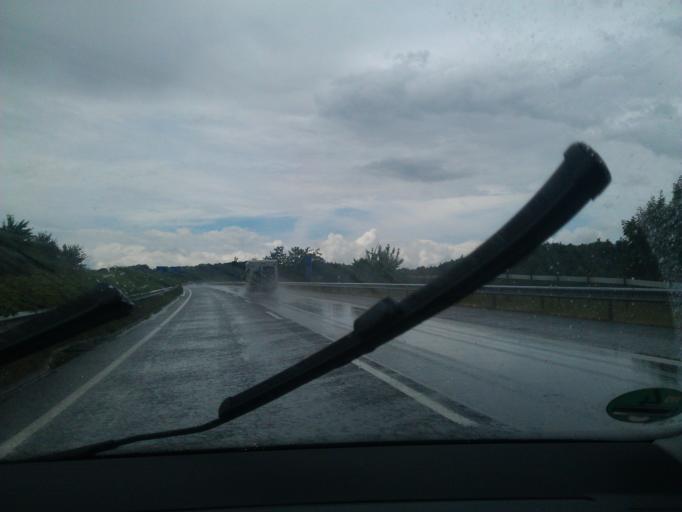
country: DE
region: Rheinland-Pfalz
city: Malbergweich
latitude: 50.0358
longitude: 6.5398
